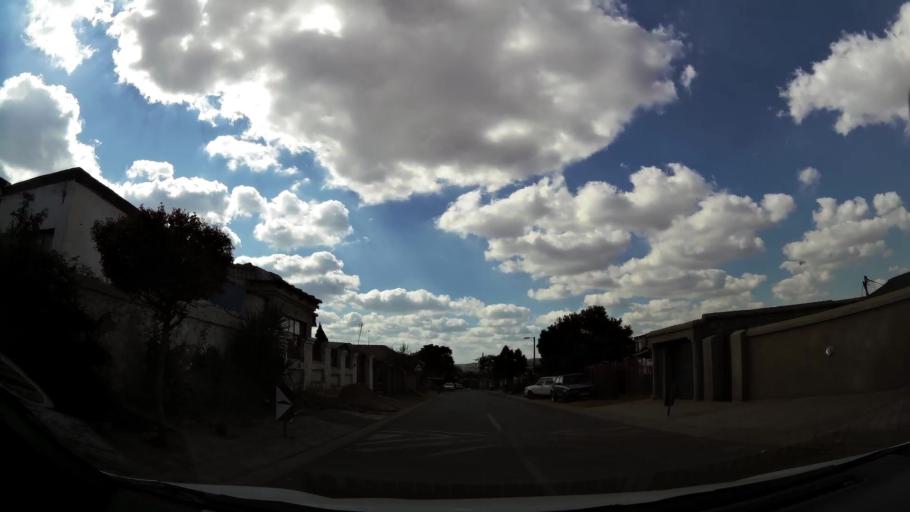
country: ZA
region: Gauteng
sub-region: City of Tshwane Metropolitan Municipality
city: Cullinan
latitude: -25.7024
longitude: 28.3960
